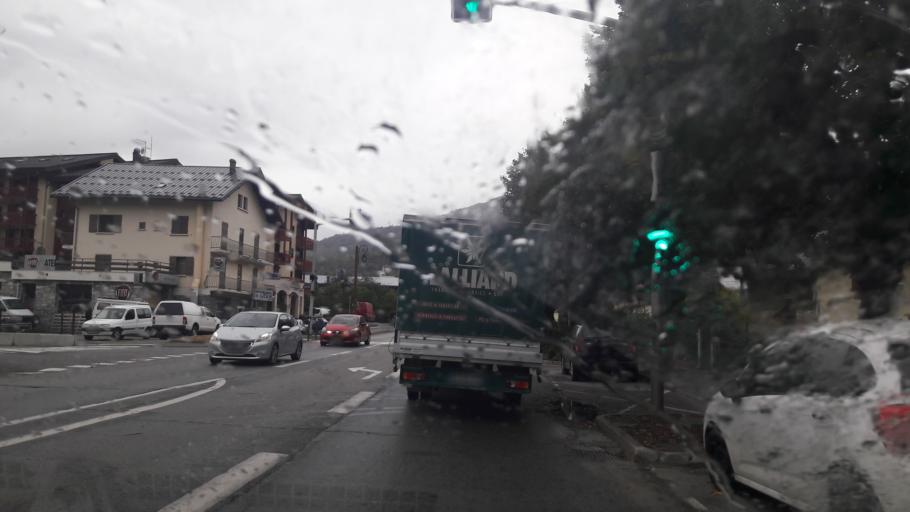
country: FR
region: Rhone-Alpes
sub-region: Departement de la Savoie
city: Bourg-Saint-Maurice
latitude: 45.6221
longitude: 6.7753
